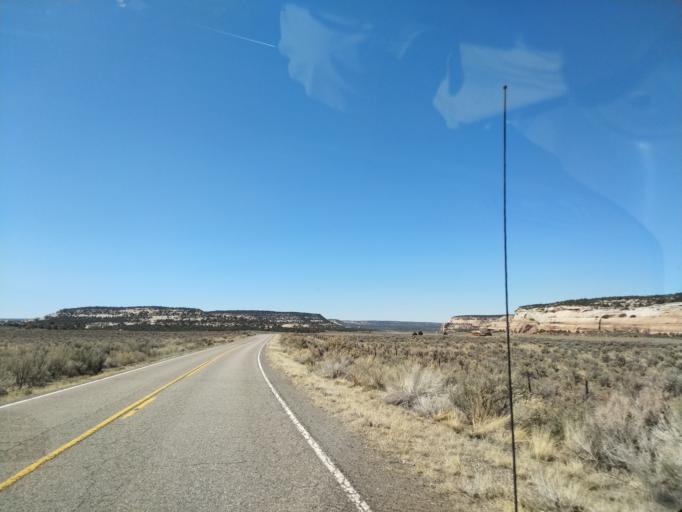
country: US
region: Colorado
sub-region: Mesa County
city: Loma
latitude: 39.0024
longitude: -108.8487
